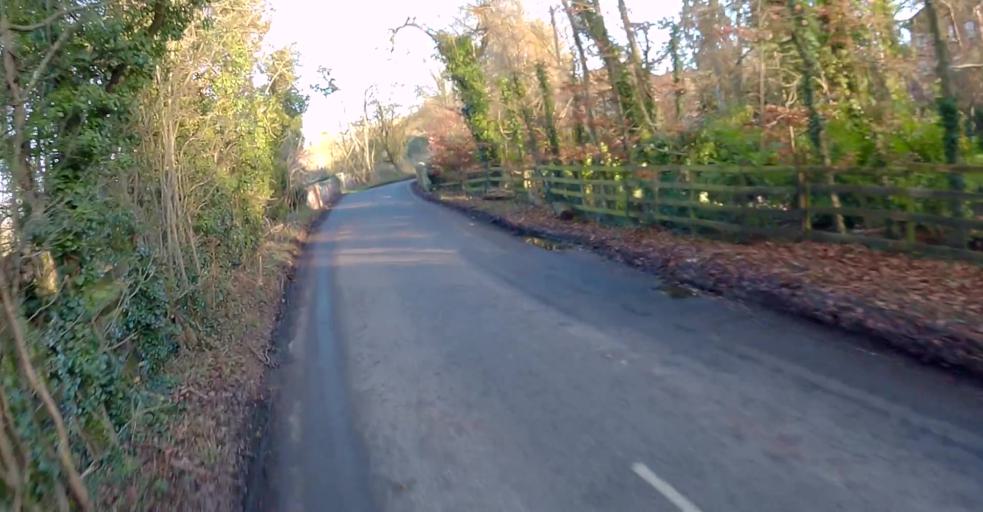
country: GB
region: England
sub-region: Hampshire
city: Old Basing
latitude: 51.2830
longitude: -1.0041
